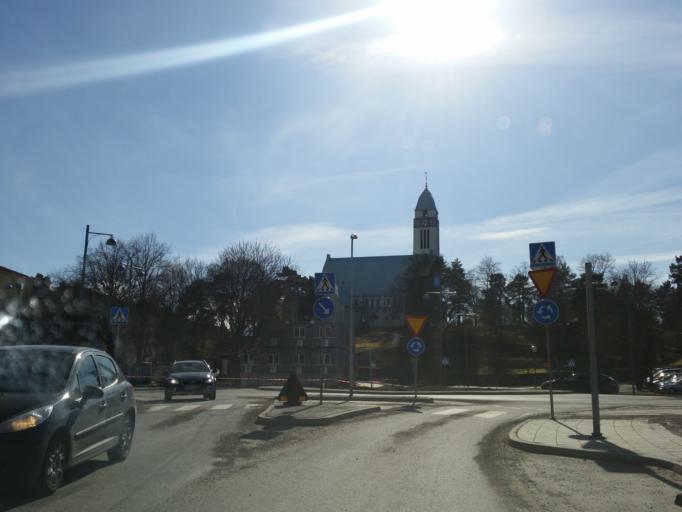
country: SE
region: Stockholm
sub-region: Sundbybergs Kommun
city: Sundbyberg
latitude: 59.3656
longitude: 17.9736
